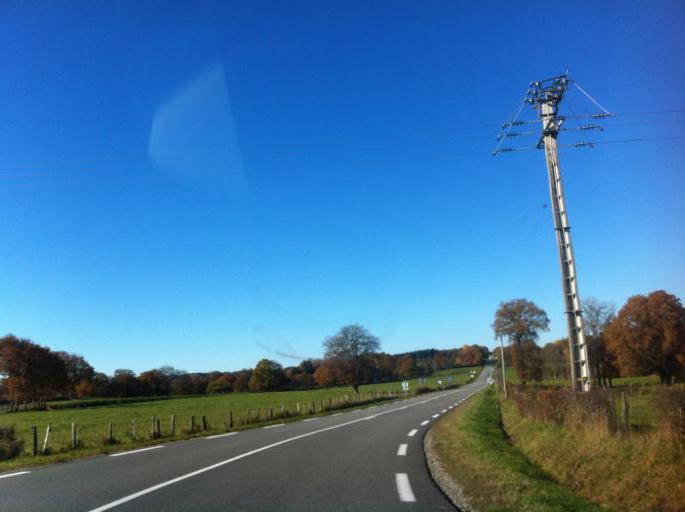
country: FR
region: Limousin
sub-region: Departement de la Creuse
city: Auzances
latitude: 45.8607
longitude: 2.5942
